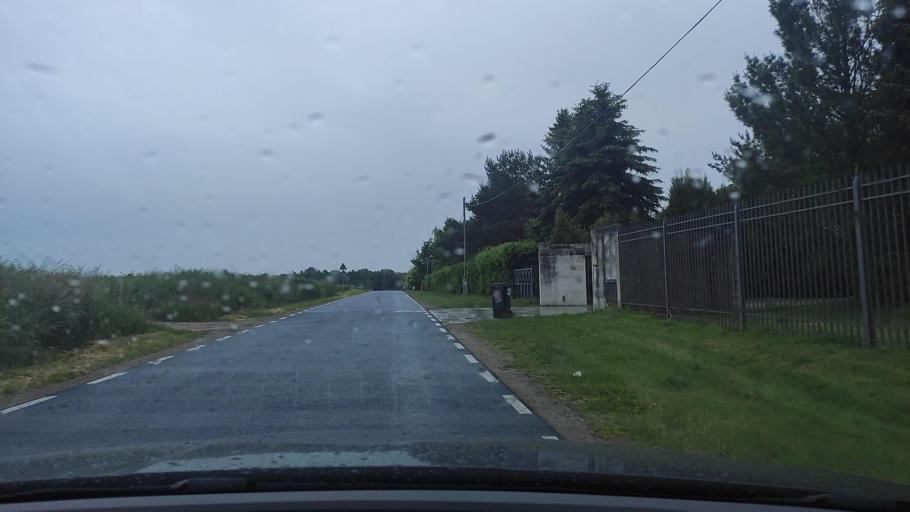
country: PL
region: Greater Poland Voivodeship
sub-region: Powiat poznanski
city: Kostrzyn
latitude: 52.4812
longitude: 17.1722
